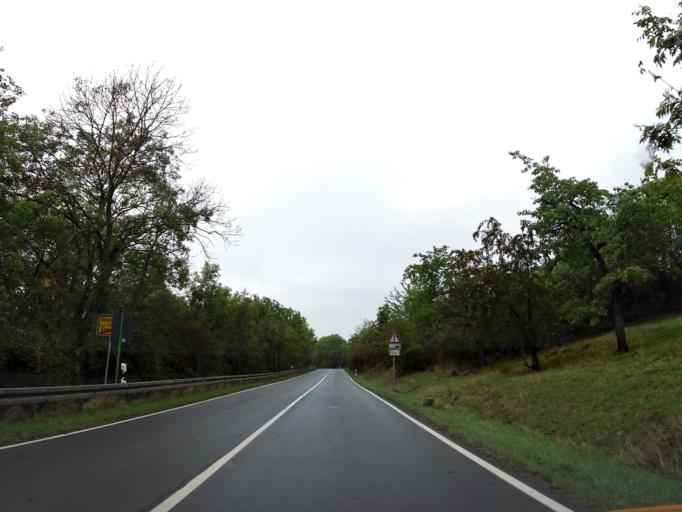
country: DE
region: Saxony-Anhalt
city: Hoym
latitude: 51.7358
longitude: 11.3337
